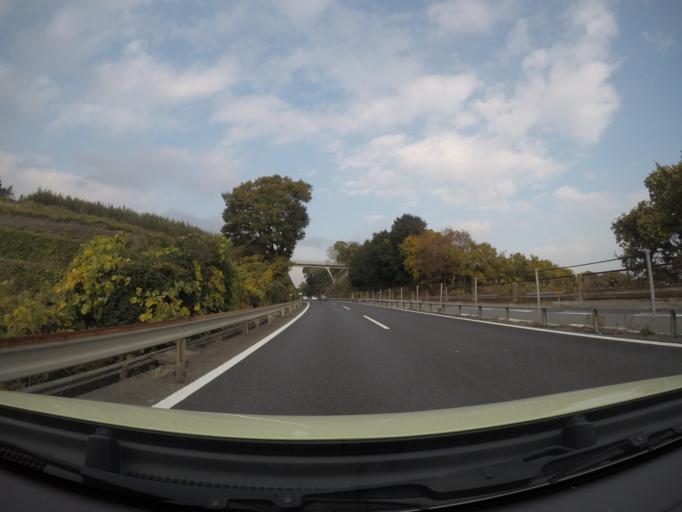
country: JP
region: Kanagawa
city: Ninomiya
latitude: 35.2981
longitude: 139.2160
